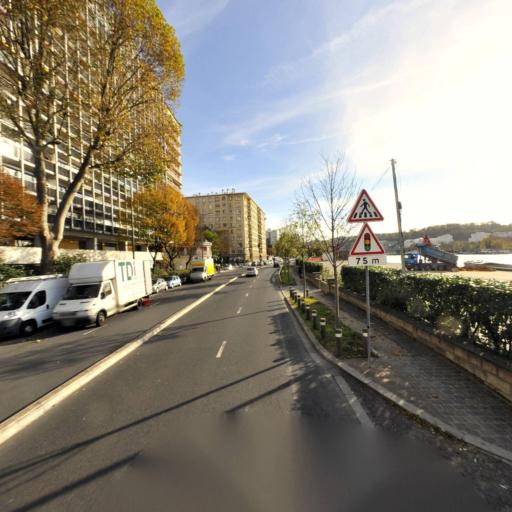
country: FR
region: Ile-de-France
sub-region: Departement des Hauts-de-Seine
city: Sevres
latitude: 48.8332
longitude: 2.2271
